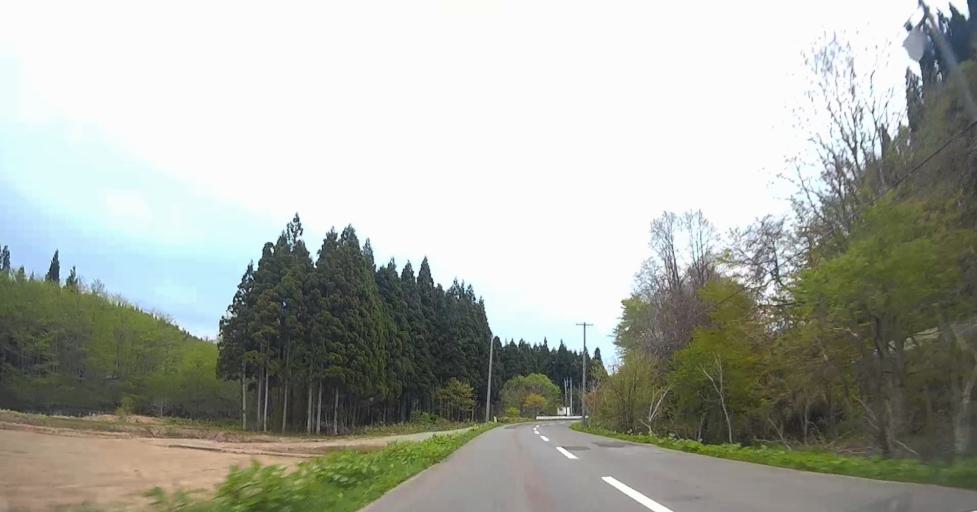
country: JP
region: Aomori
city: Goshogawara
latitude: 41.1214
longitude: 140.5228
